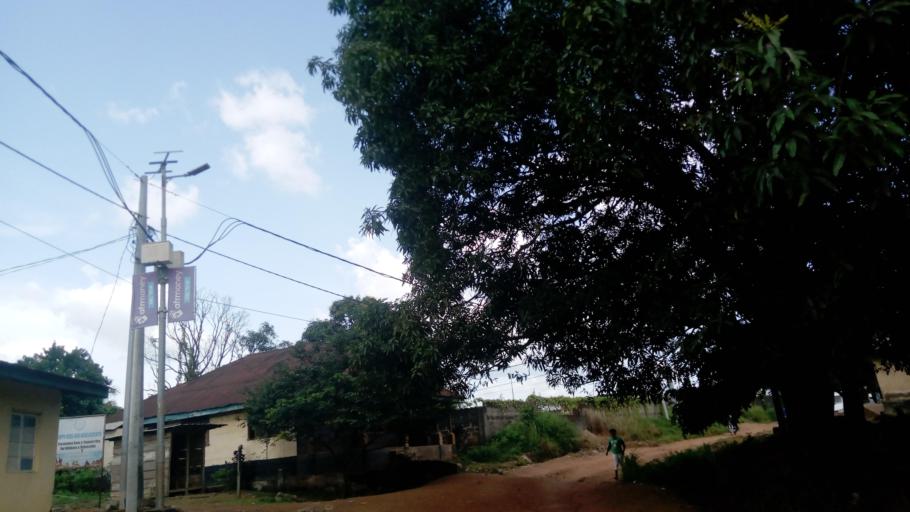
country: SL
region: Northern Province
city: Makeni
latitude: 8.8935
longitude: -12.0461
